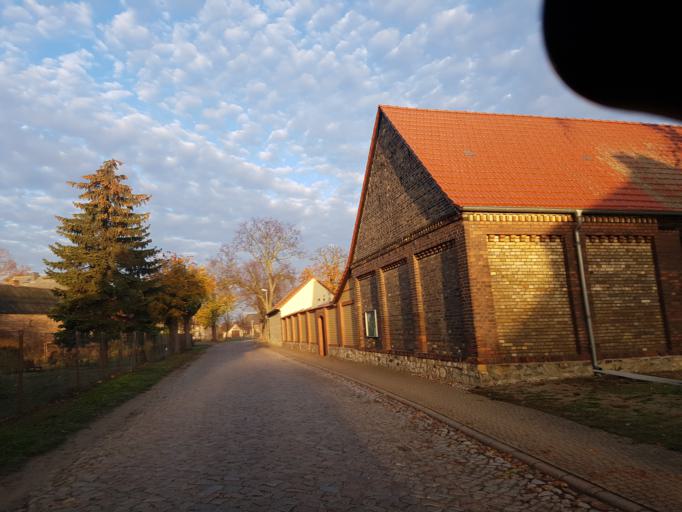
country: DE
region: Saxony-Anhalt
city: Elster
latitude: 51.8478
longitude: 12.8387
